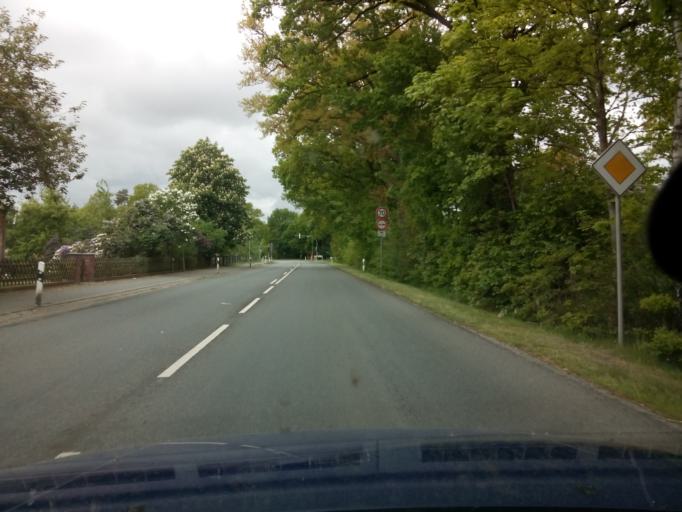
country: DE
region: Lower Saxony
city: Schwanewede
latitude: 53.2308
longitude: 8.6720
